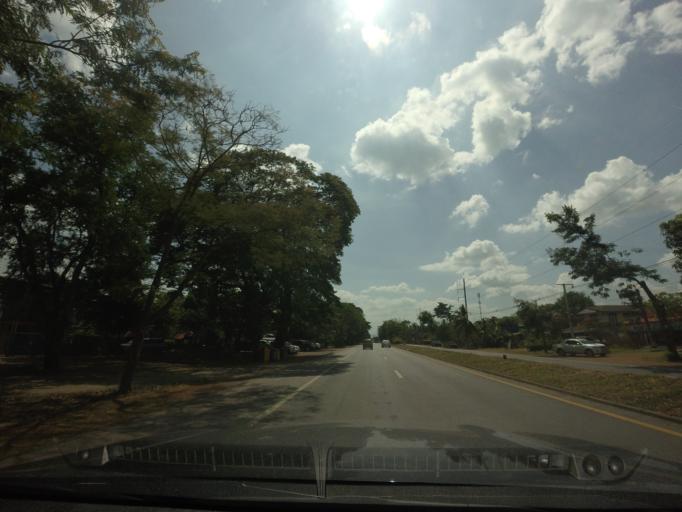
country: TH
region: Phetchabun
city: Nong Phai
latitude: 15.9558
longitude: 101.0422
